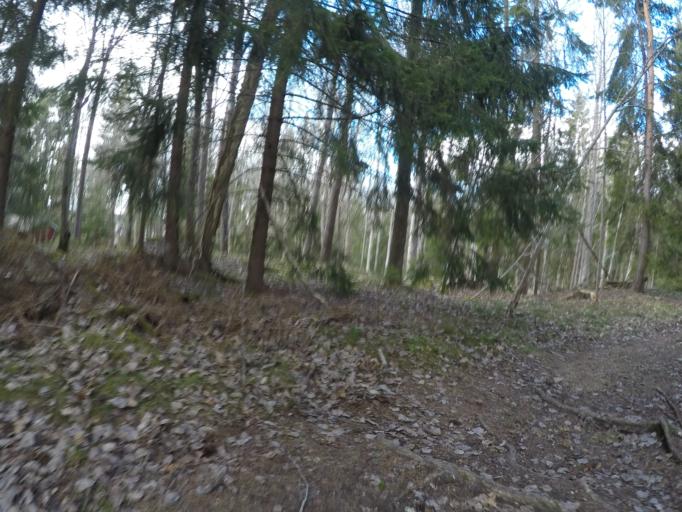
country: SE
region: Soedermanland
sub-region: Eskilstuna Kommun
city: Kvicksund
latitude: 59.4934
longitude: 16.2811
